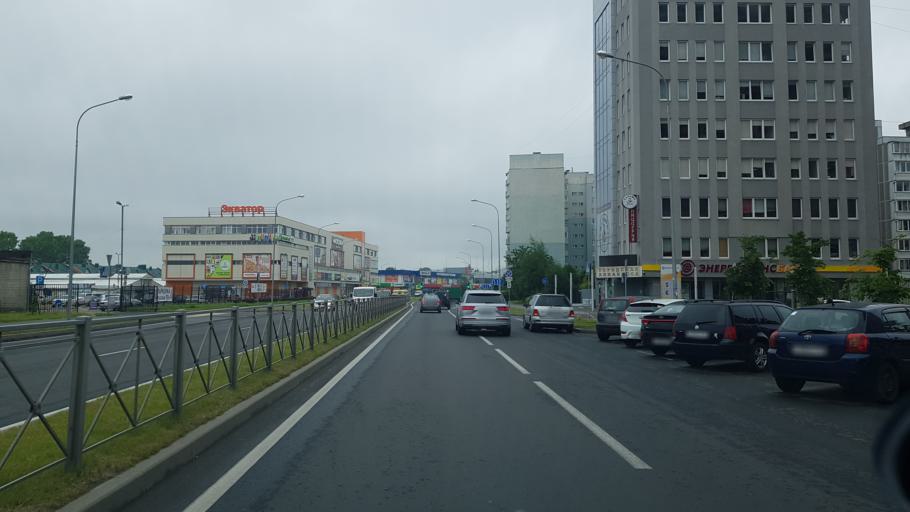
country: RU
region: Kaliningrad
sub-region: Gorod Kaliningrad
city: Kaliningrad
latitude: 54.7372
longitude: 20.4908
